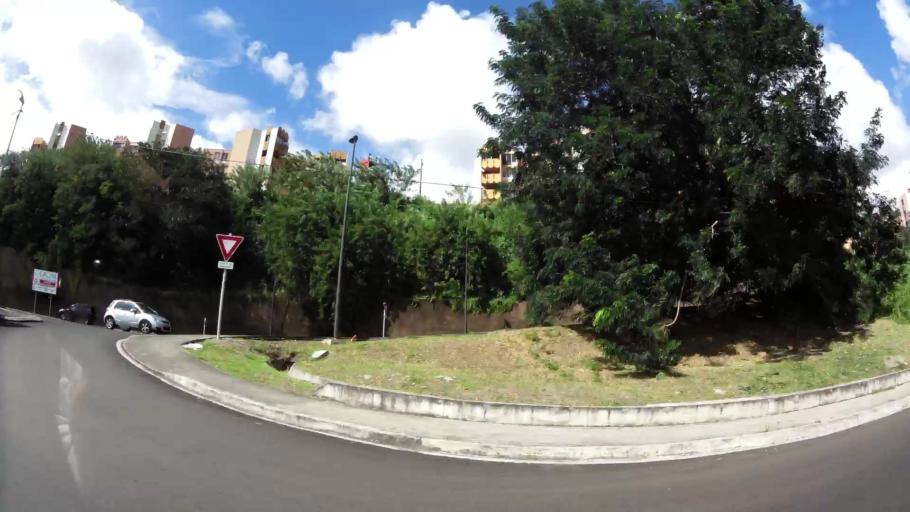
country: MQ
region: Martinique
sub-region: Martinique
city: Fort-de-France
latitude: 14.6036
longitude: -61.0619
